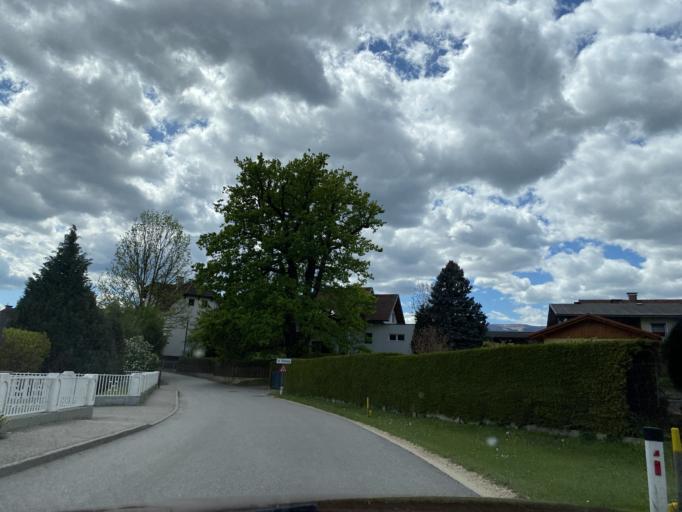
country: AT
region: Carinthia
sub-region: Politischer Bezirk Wolfsberg
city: Wolfsberg
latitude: 46.8277
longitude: 14.8308
